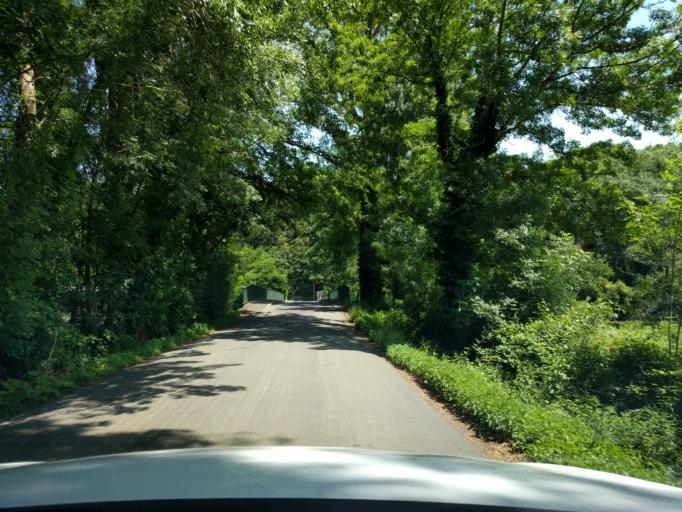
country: FR
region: Poitou-Charentes
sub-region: Departement des Deux-Sevres
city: Niort
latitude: 46.3551
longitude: -0.4572
